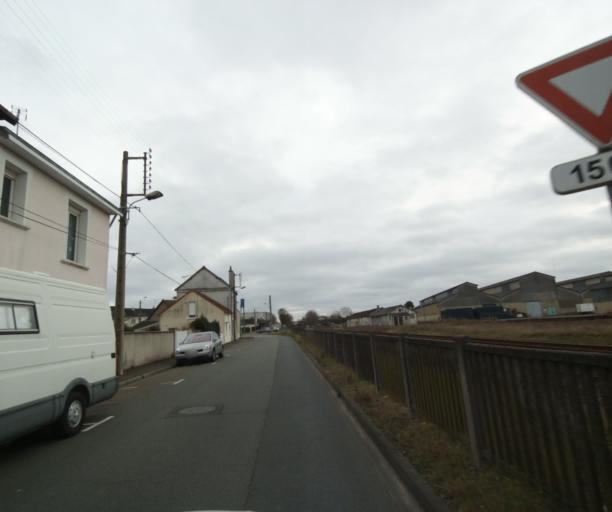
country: FR
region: Pays de la Loire
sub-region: Departement de la Sarthe
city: Le Mans
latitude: 47.9752
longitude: 0.1996
